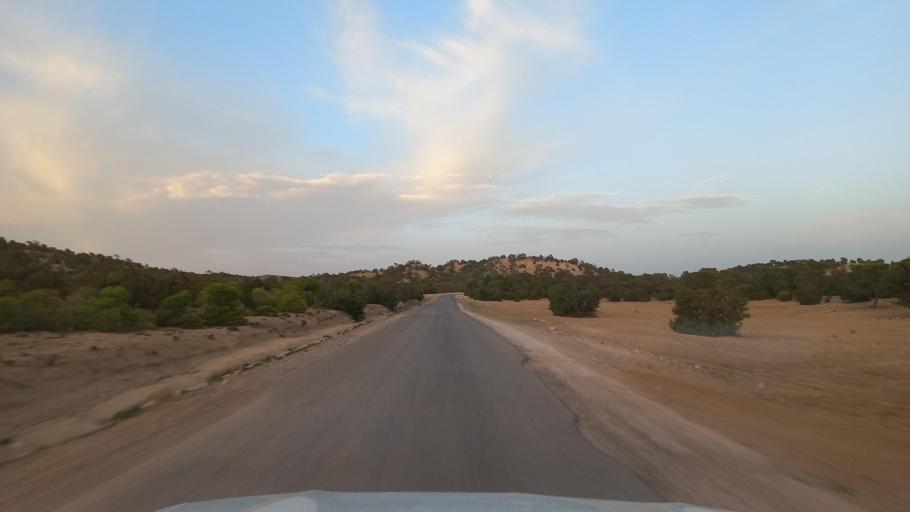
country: TN
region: Al Qasrayn
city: Sbiba
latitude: 35.4106
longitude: 8.9546
